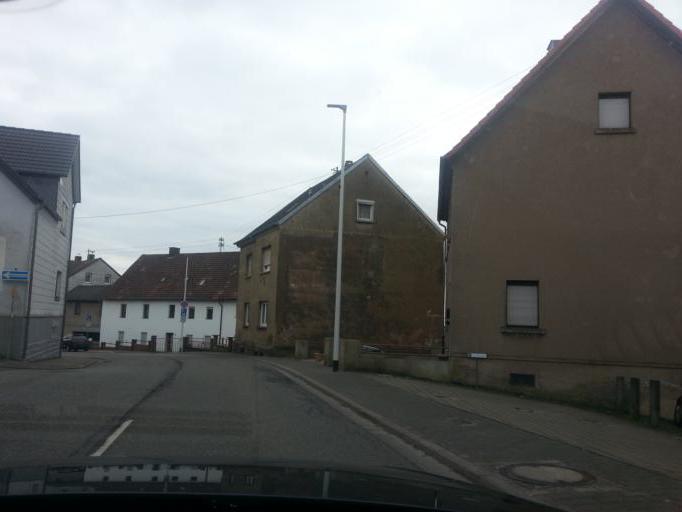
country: DE
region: Saarland
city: Bexbach
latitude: 49.3769
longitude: 7.2554
